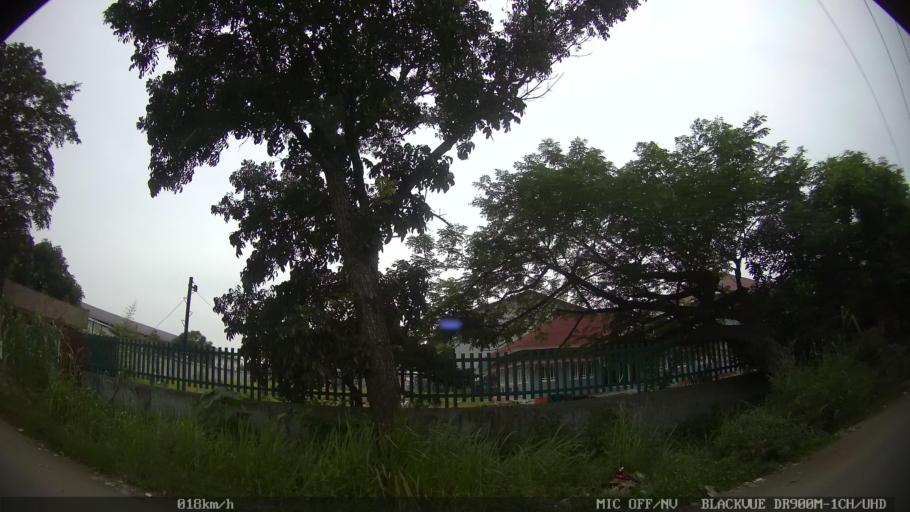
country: ID
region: North Sumatra
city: Deli Tua
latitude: 3.5377
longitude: 98.7295
